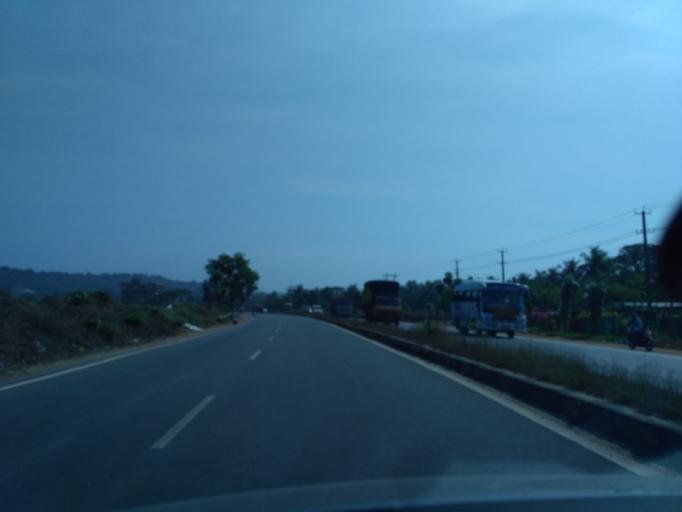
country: IN
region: Karnataka
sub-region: Dakshina Kannada
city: Ullal
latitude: 12.8665
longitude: 74.9102
